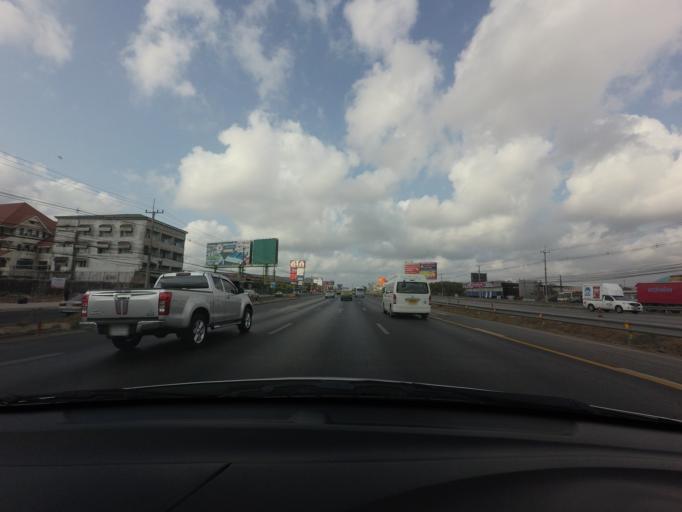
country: TH
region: Bangkok
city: Bang Bon
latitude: 13.6045
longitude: 100.3722
